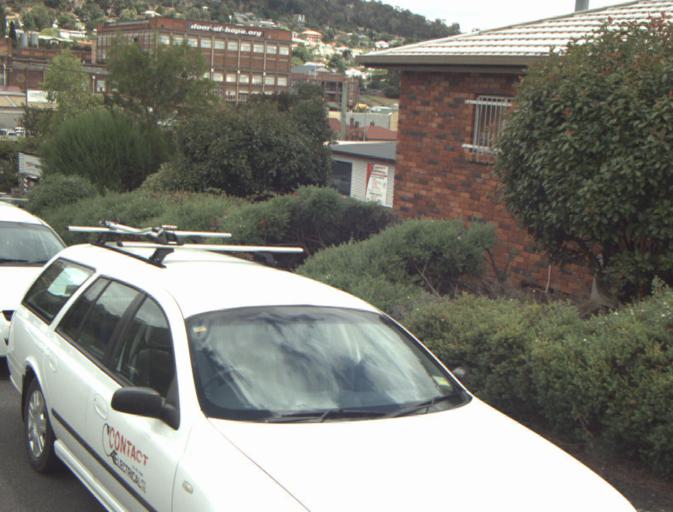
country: AU
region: Tasmania
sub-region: Launceston
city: West Launceston
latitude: -41.4533
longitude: 147.1427
